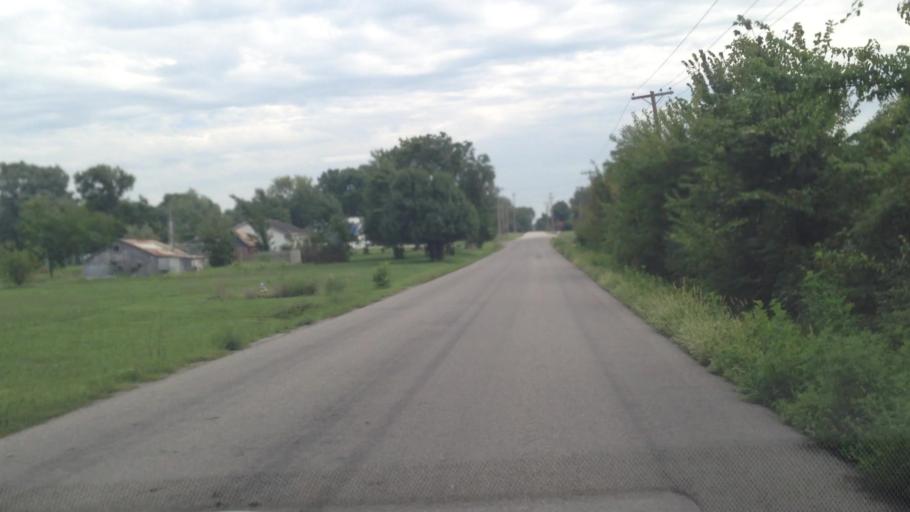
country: US
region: Kansas
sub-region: Crawford County
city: Girard
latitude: 37.4992
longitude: -94.8450
